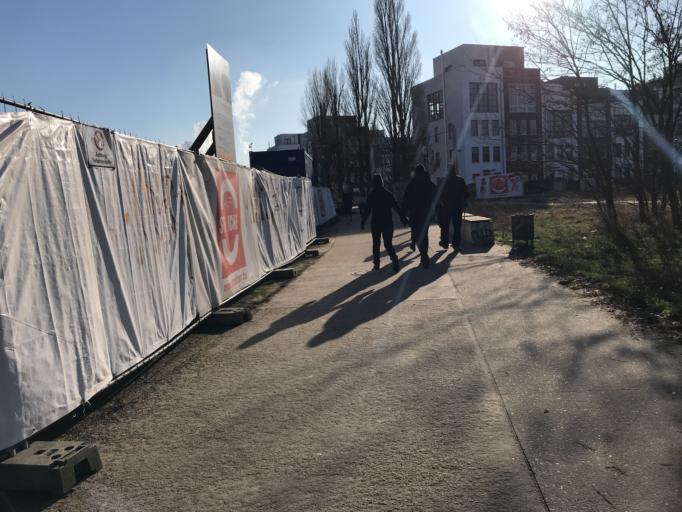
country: DE
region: Berlin
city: Treptow Bezirk
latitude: 52.4990
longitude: 13.4693
